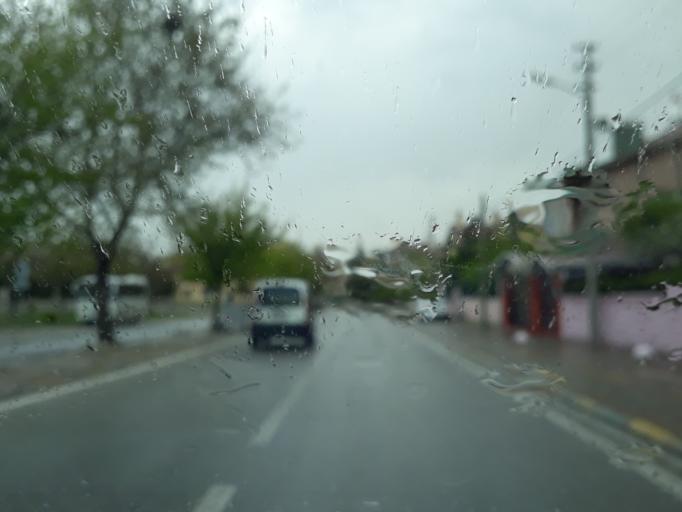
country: TR
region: Konya
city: Selcuklu
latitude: 37.9224
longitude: 32.4913
